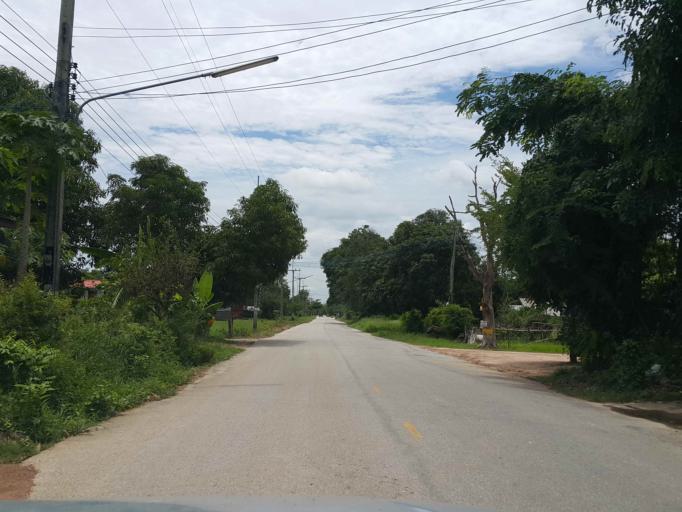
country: TH
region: Sukhothai
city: Ban Na
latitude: 17.0062
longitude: 99.7065
